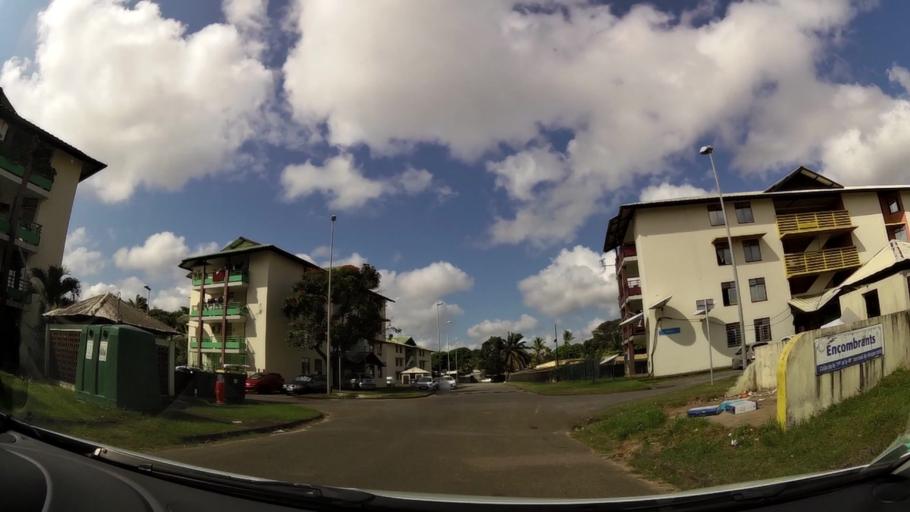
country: GF
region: Guyane
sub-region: Guyane
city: Cayenne
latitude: 4.9351
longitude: -52.3163
